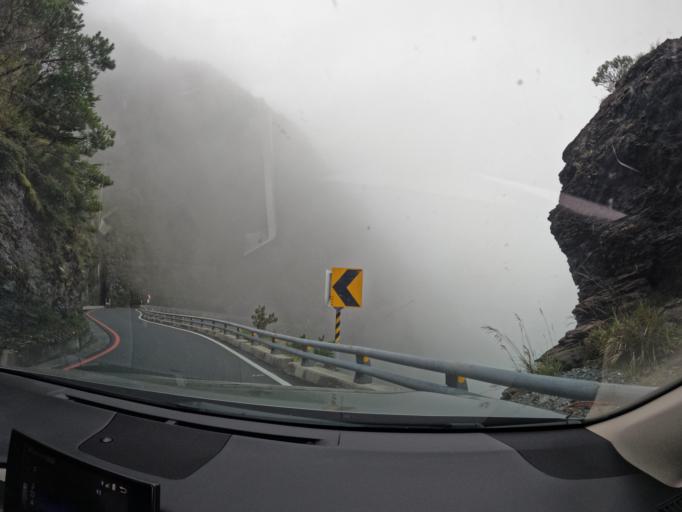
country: TW
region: Taiwan
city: Lugu
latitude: 23.2648
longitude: 120.9770
